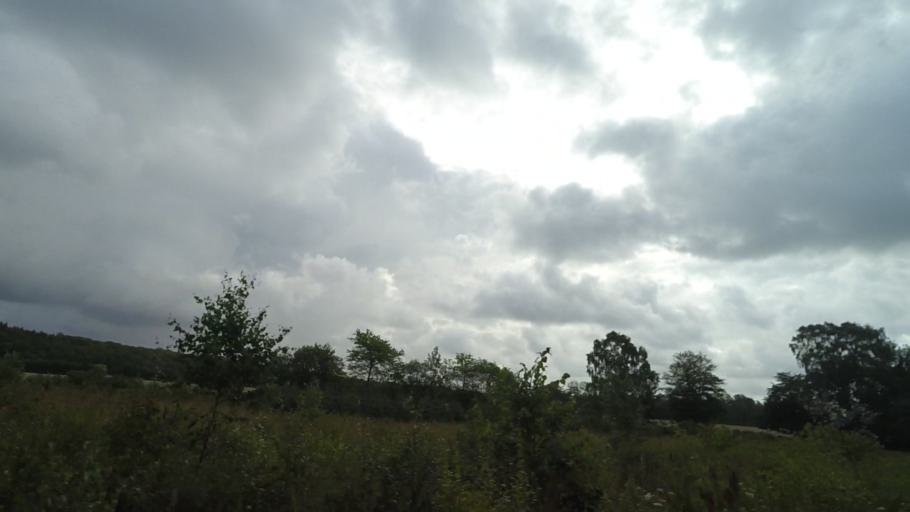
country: DK
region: Central Jutland
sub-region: Syddjurs Kommune
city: Ryomgard
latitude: 56.4422
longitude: 10.5597
